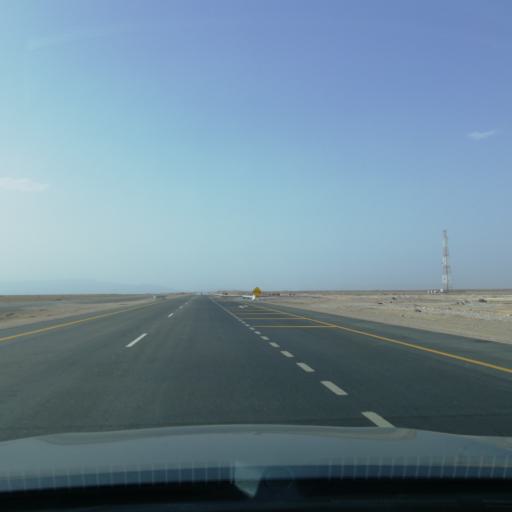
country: OM
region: Muhafazat ad Dakhiliyah
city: Adam
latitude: 22.1390
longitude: 57.5242
